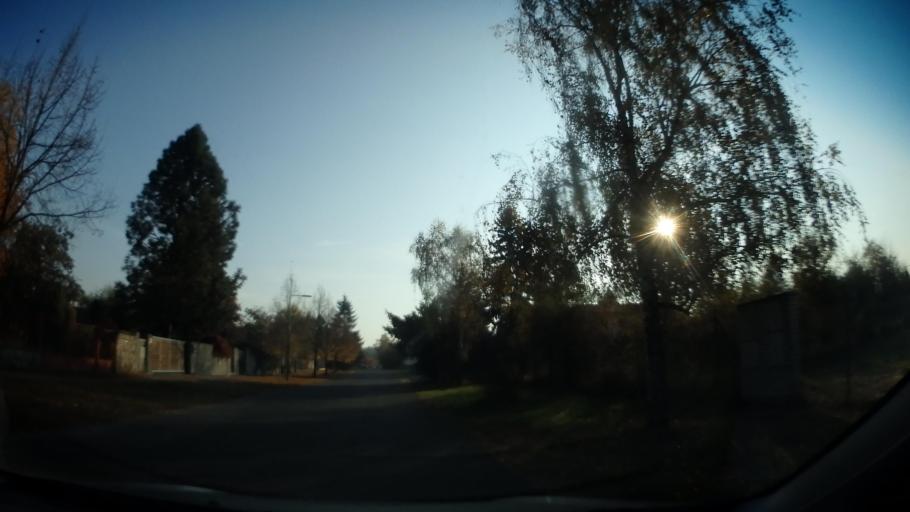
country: CZ
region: Central Bohemia
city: Sestajovice
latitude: 50.1012
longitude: 14.6847
